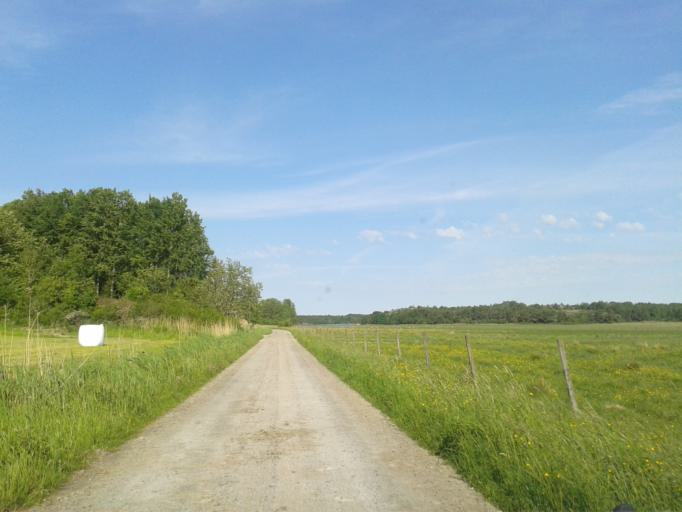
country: SE
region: Vaestra Goetaland
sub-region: Stromstads Kommun
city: Stroemstad
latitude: 58.8628
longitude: 11.2177
